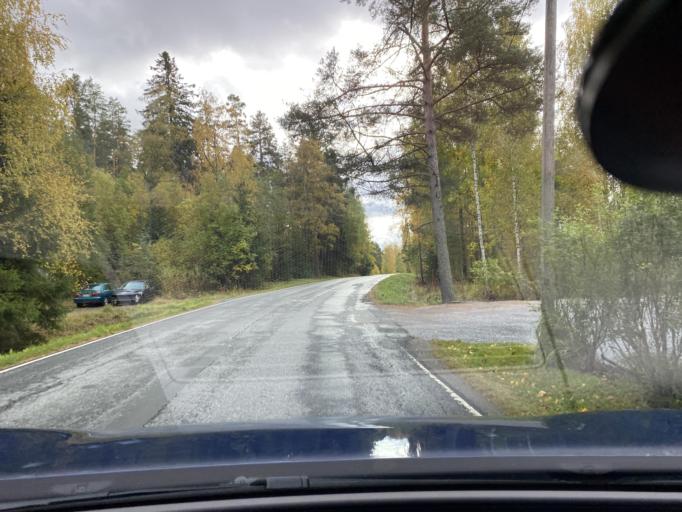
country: FI
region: Pirkanmaa
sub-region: Tampere
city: Nokia
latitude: 61.4958
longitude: 23.3450
